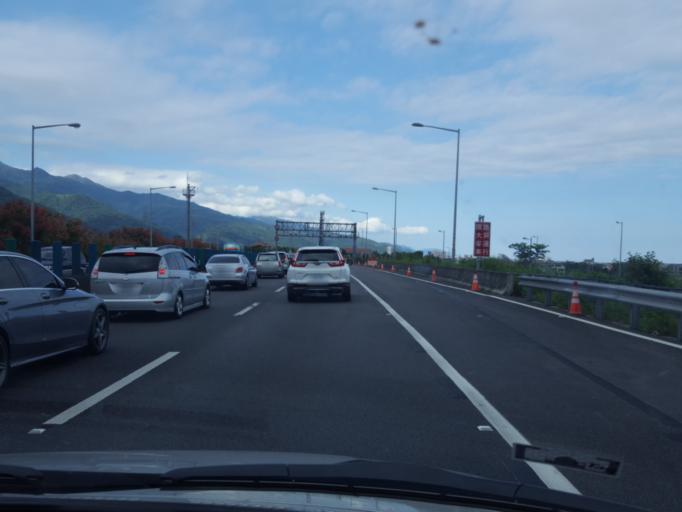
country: TW
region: Taiwan
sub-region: Yilan
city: Yilan
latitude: 24.8255
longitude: 121.7884
